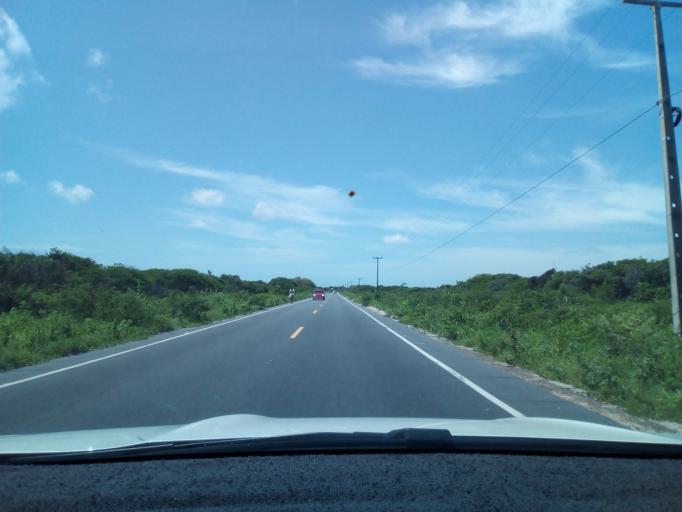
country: BR
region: Ceara
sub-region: Aracati
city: Aracati
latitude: -4.3918
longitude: -37.8739
